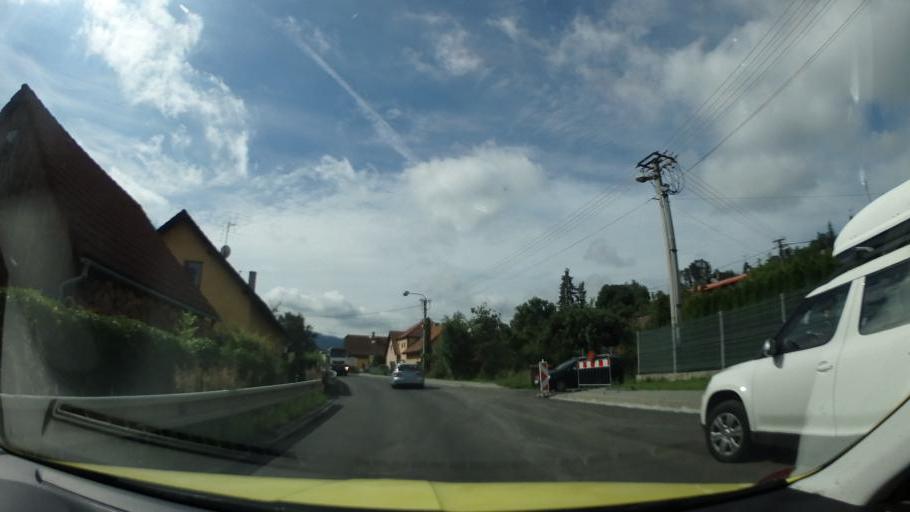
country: CZ
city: Hodslavice
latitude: 49.5510
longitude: 18.0259
